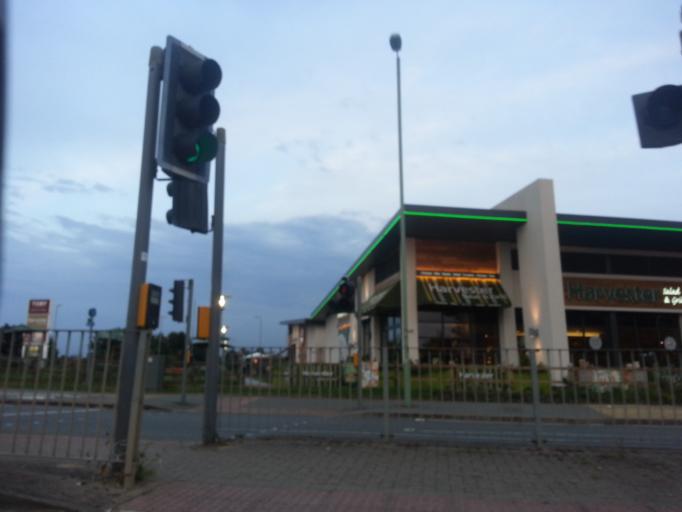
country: GB
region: England
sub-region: Suffolk
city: Kesgrave
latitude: 52.0297
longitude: 1.2012
